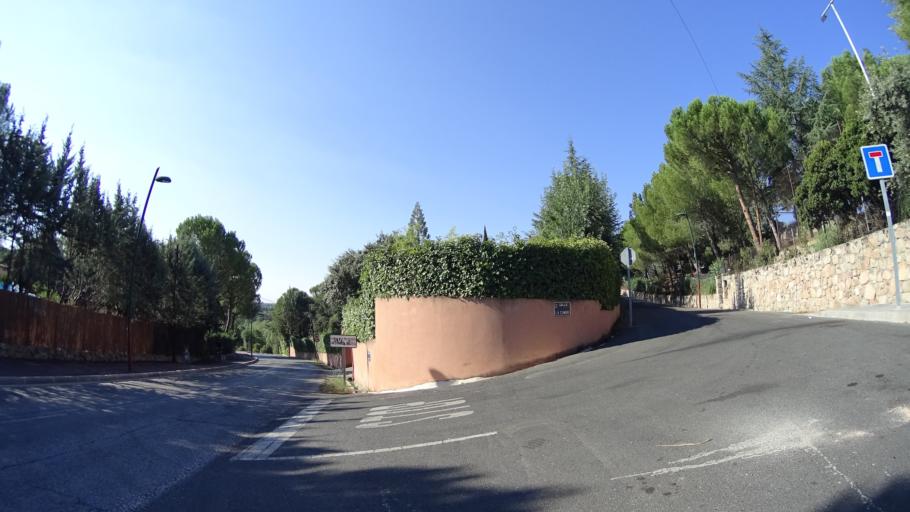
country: ES
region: Madrid
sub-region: Provincia de Madrid
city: Las Matas
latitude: 40.5739
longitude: -3.8966
